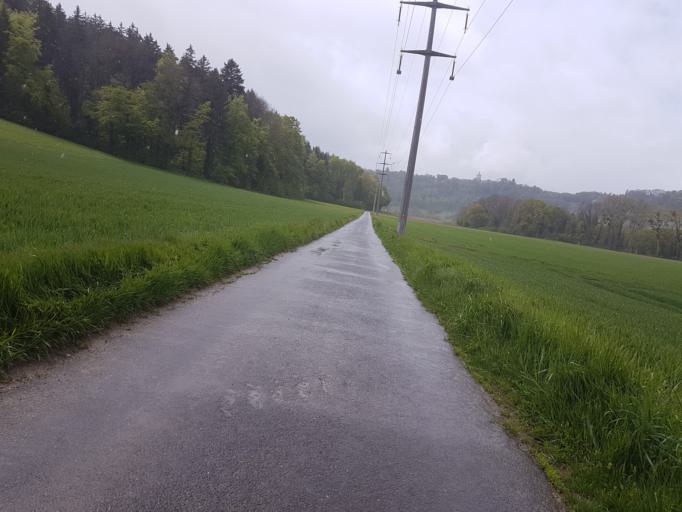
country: CH
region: Vaud
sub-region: Gros-de-Vaud District
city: Penthalaz
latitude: 46.6208
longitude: 6.5275
